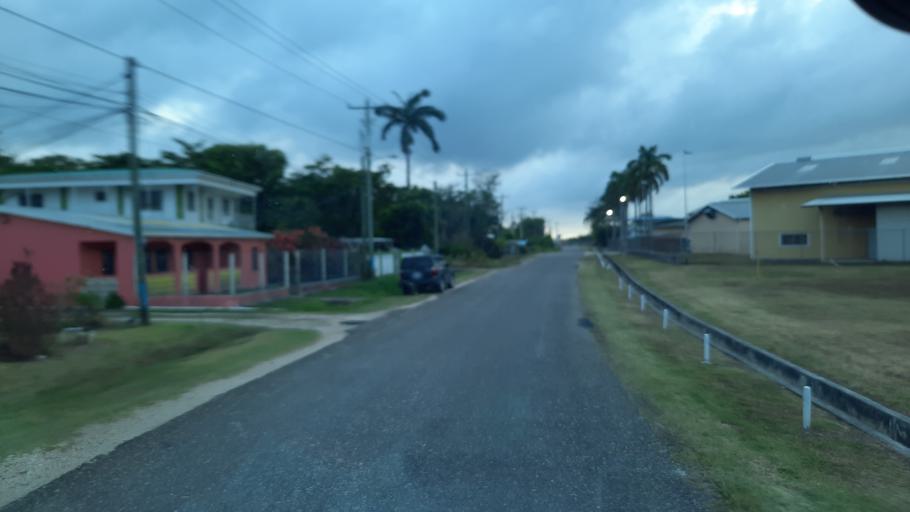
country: BZ
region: Belize
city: Belize City
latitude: 17.5442
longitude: -88.2975
